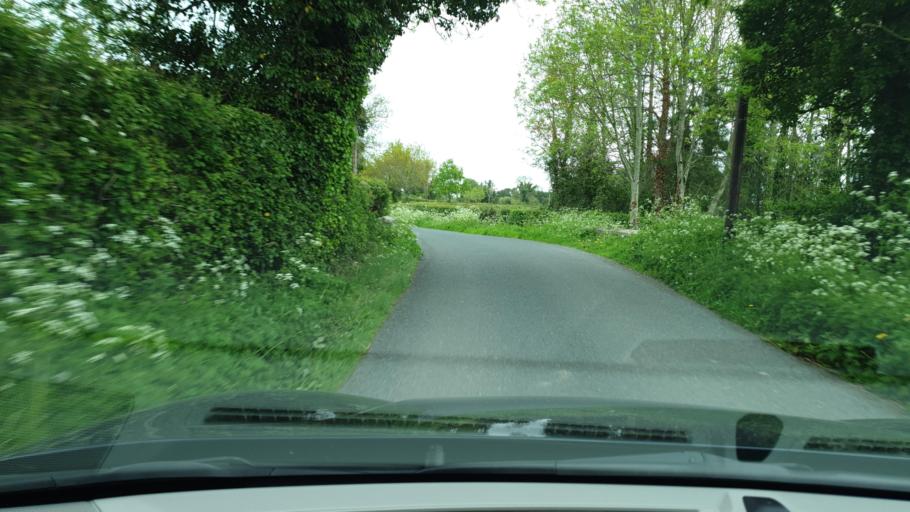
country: IE
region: Leinster
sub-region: An Mhi
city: Dunboyne
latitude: 53.4480
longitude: -6.5106
